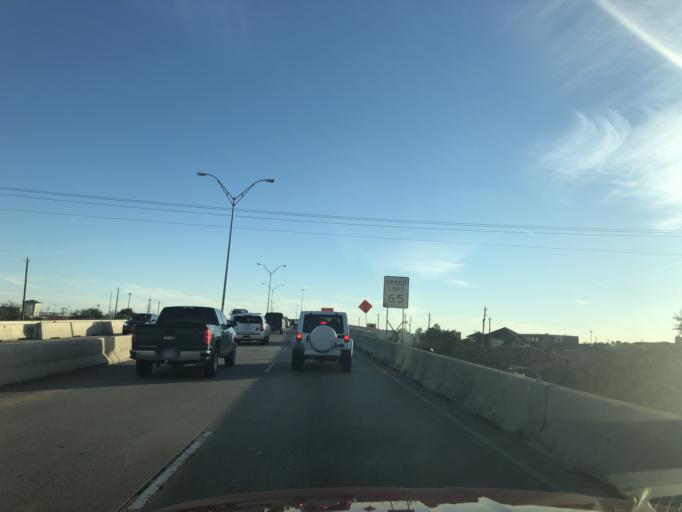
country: US
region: Texas
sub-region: Harris County
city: Deer Park
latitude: 29.6604
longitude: -95.1564
